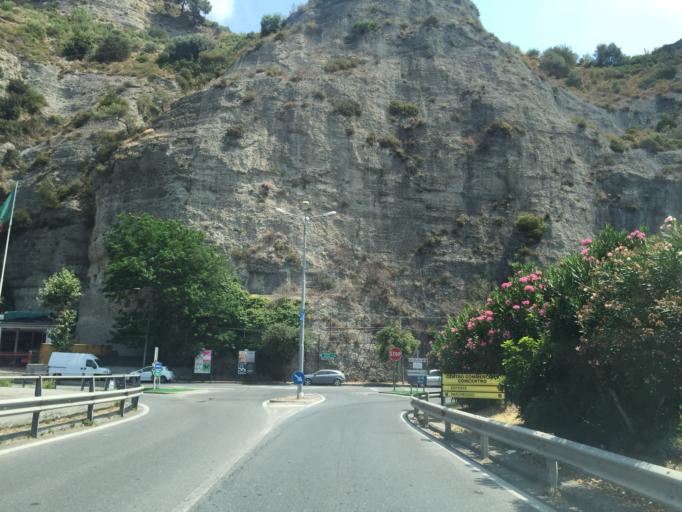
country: IT
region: Liguria
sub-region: Provincia di Imperia
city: Ventimiglia
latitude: 43.8004
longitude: 7.5993
